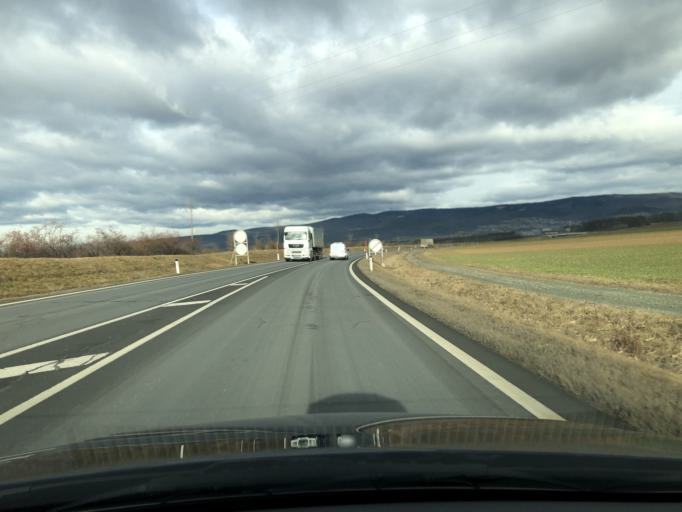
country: AT
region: Burgenland
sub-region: Politischer Bezirk Oberwart
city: Schachendorf
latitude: 47.2630
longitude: 16.4498
